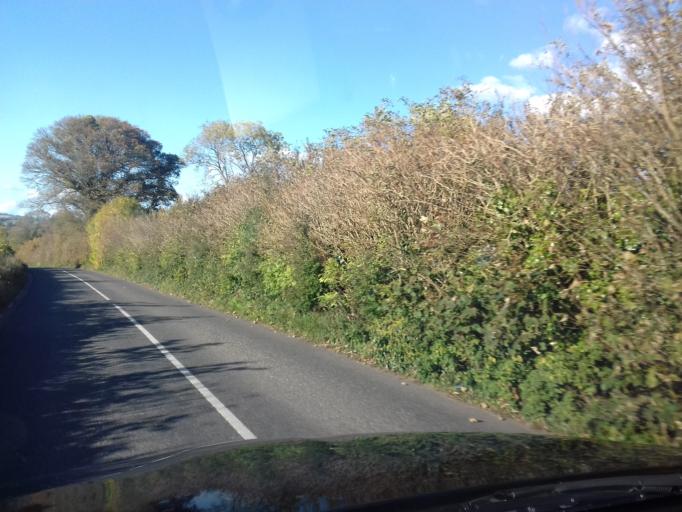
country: IE
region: Leinster
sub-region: Lu
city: Tullyallen
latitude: 53.7076
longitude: -6.4093
